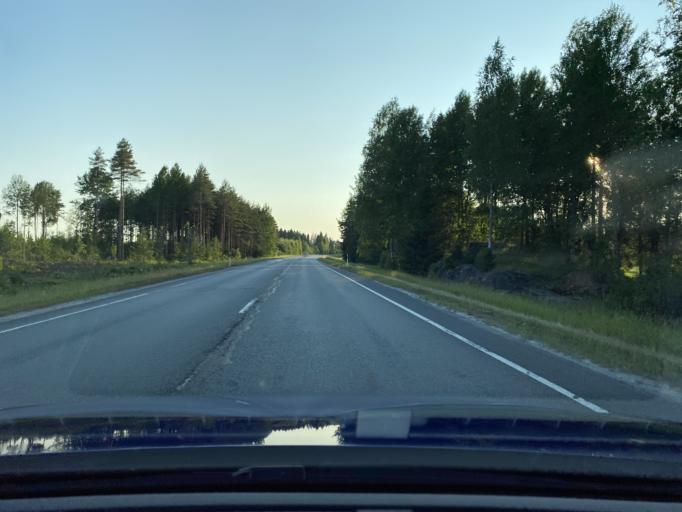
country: FI
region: Haeme
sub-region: Forssa
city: Tammela
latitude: 60.8261
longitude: 23.7526
